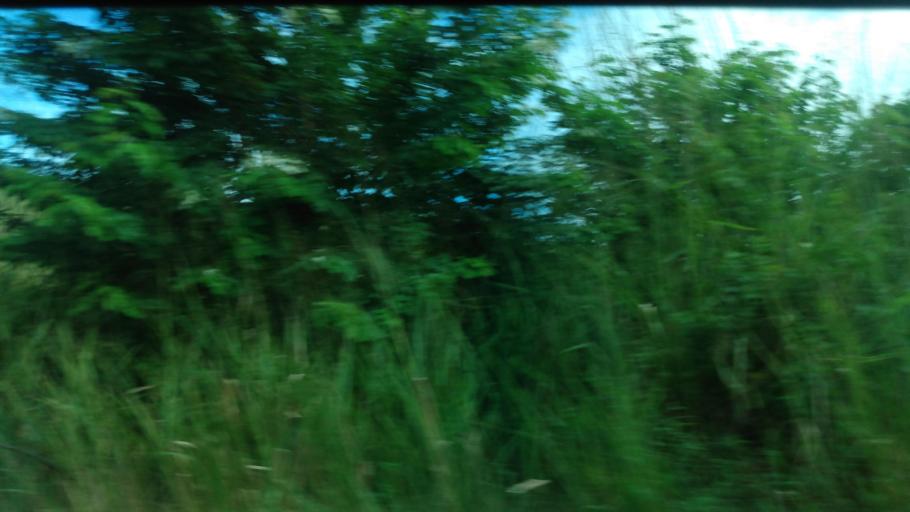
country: BR
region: Pernambuco
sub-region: Catende
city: Catende
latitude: -8.6896
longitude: -35.7042
